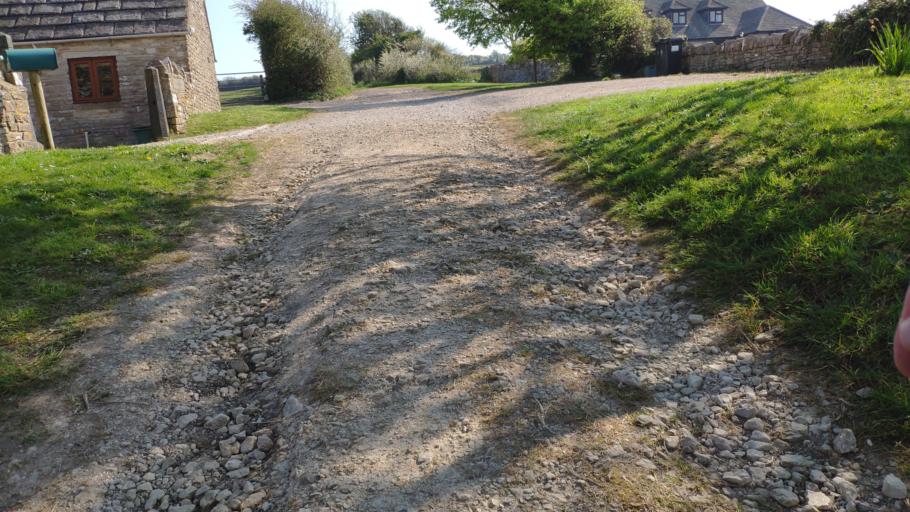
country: GB
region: England
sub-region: Dorset
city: Swanage
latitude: 50.6002
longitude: -1.9609
